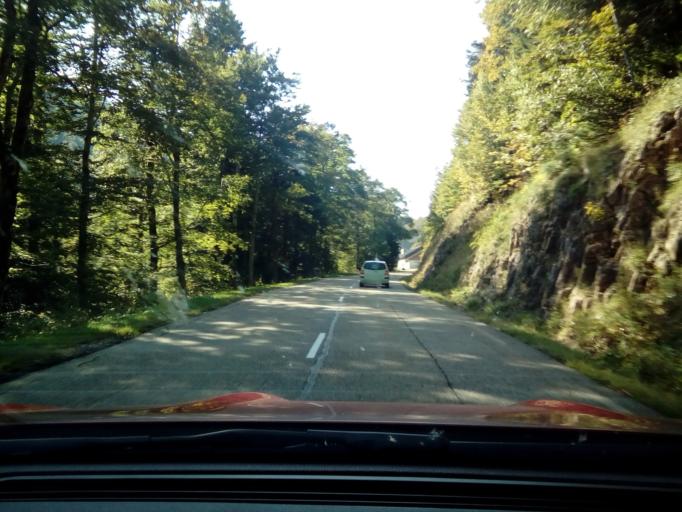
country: FR
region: Rhone-Alpes
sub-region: Departement de la Drome
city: Die
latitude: 44.8446
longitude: 5.4049
